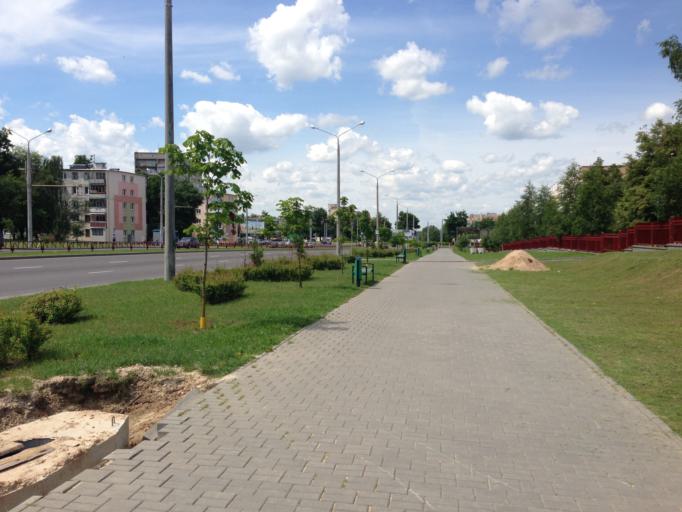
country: BY
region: Grodnenskaya
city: Hrodna
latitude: 53.7002
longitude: 23.8233
